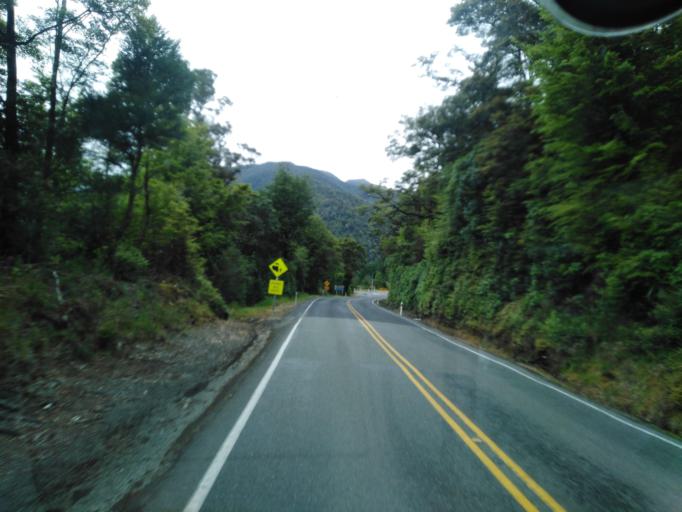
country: NZ
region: Tasman
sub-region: Tasman District
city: Wakefield
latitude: -41.7113
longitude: 172.5594
